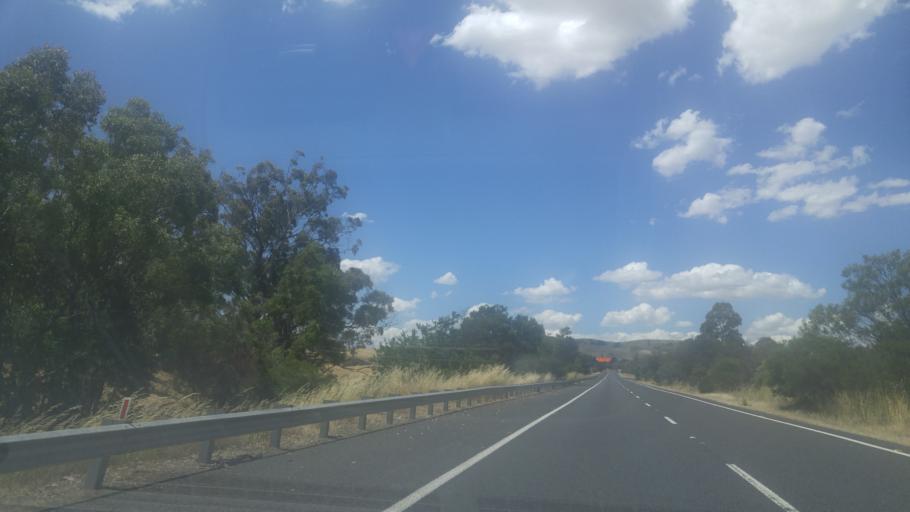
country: AU
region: New South Wales
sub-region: Yass Valley
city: Yass
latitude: -34.7862
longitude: 148.7033
